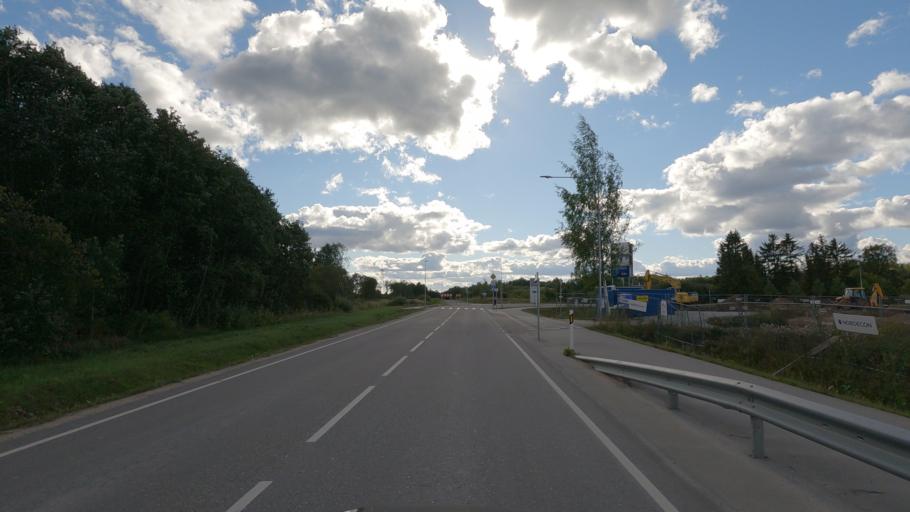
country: EE
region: Jaervamaa
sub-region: Paide linn
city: Paide
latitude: 58.8763
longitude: 25.5544
